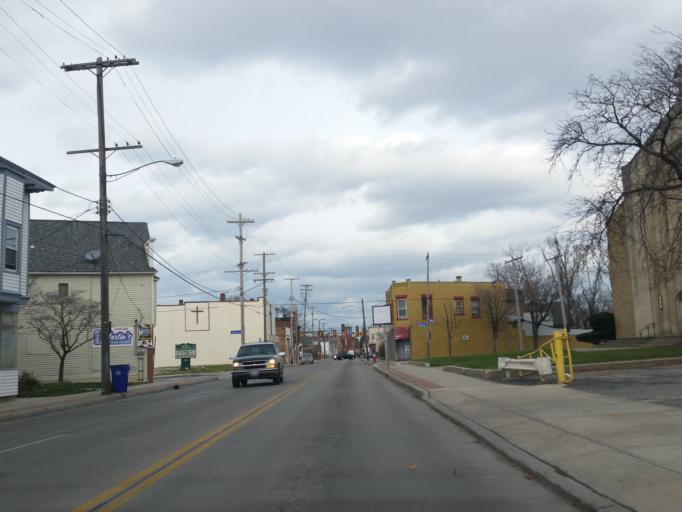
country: US
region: Ohio
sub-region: Cuyahoga County
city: Brooklyn
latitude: 41.4620
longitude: -81.7105
